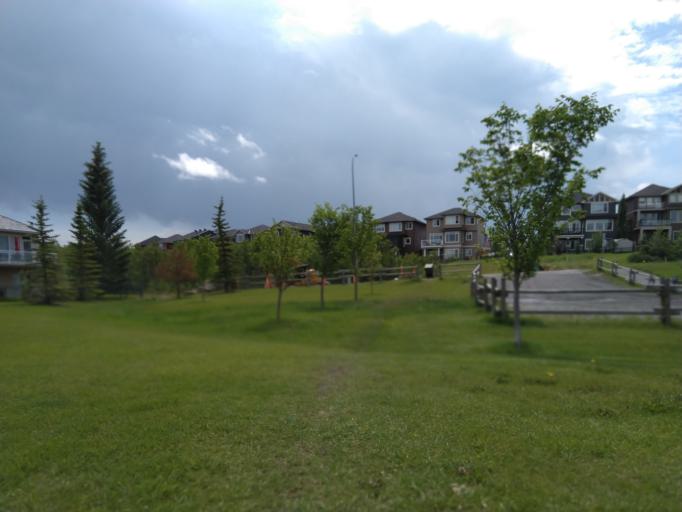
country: CA
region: Alberta
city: Cochrane
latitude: 51.1849
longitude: -114.5047
